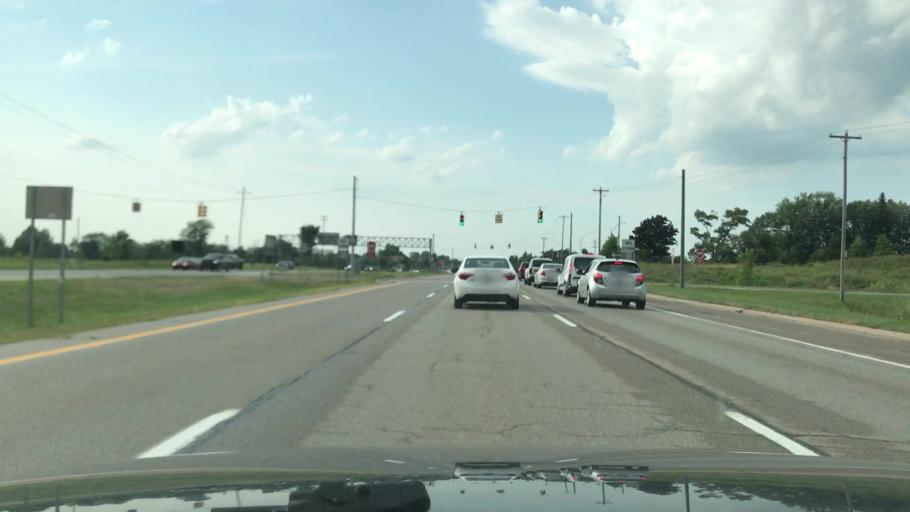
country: US
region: Michigan
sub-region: Kent County
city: Caledonia
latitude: 42.8520
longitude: -85.5399
